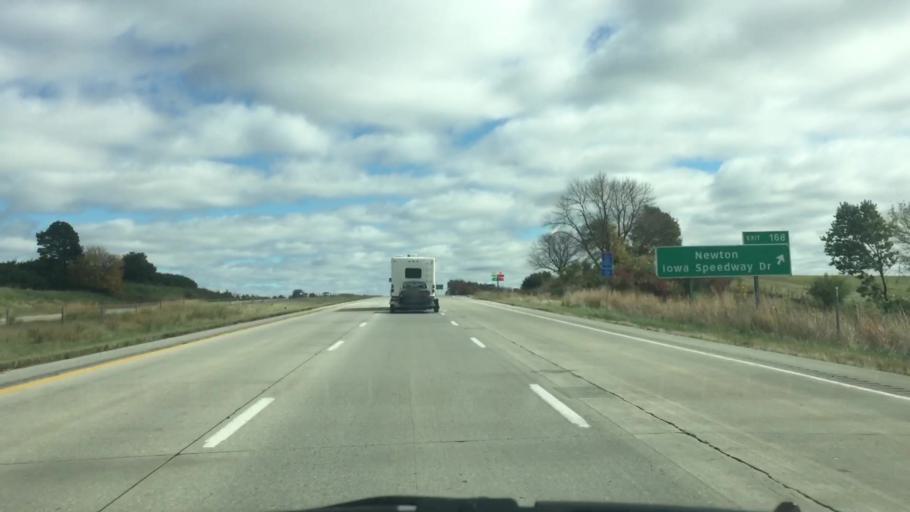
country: US
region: Iowa
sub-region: Jasper County
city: Newton
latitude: 41.6826
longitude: -93.0085
